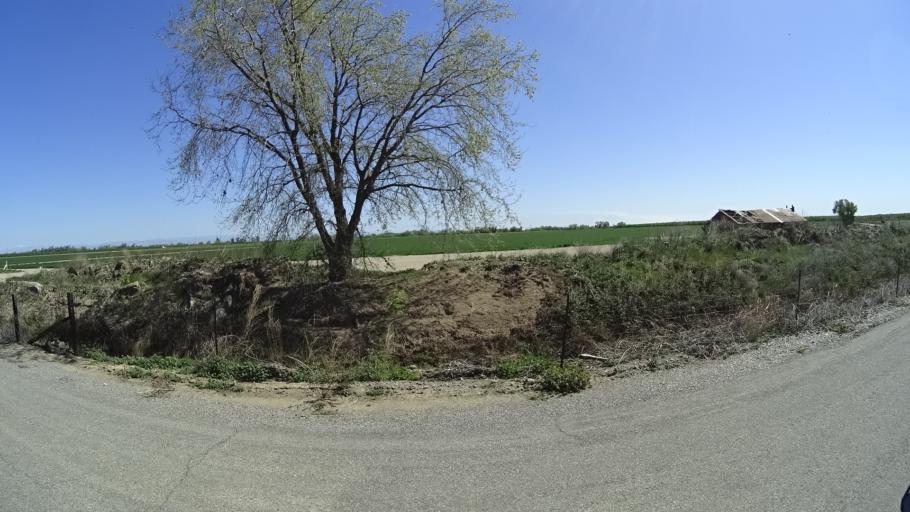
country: US
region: California
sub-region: Glenn County
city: Orland
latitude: 39.6638
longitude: -122.2346
